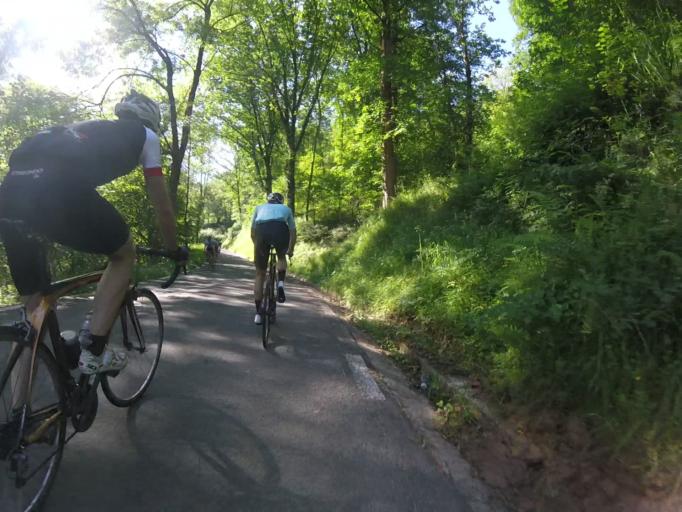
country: ES
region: Basque Country
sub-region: Provincia de Guipuzcoa
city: Beizama
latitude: 43.1396
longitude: -2.2198
